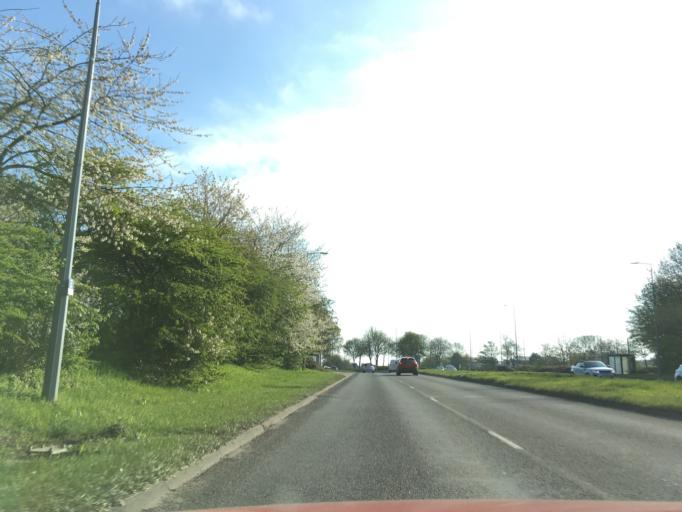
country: GB
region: England
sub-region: Milton Keynes
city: Bradwell
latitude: 52.0570
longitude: -0.7753
